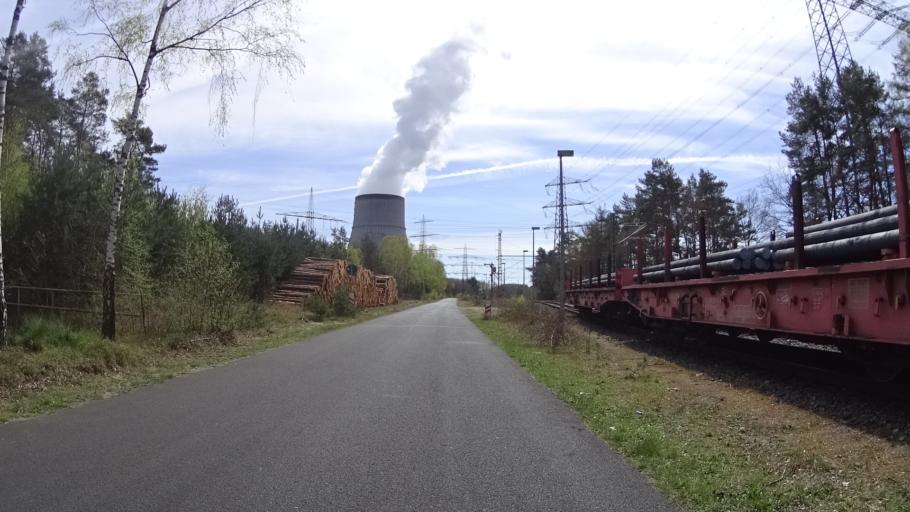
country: DE
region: Lower Saxony
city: Lingen
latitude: 52.4792
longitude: 7.3106
